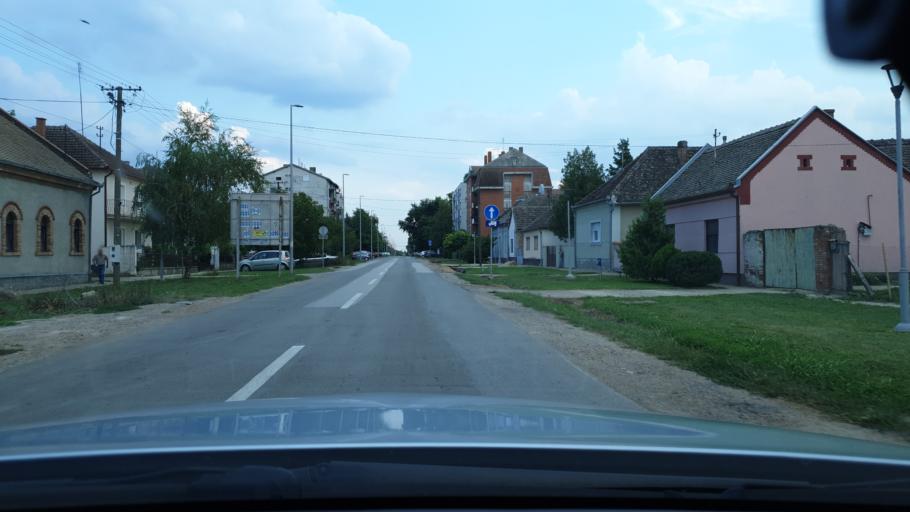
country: RS
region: Autonomna Pokrajina Vojvodina
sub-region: Juznobanatski Okrug
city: Plandiste
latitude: 45.2309
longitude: 21.1192
